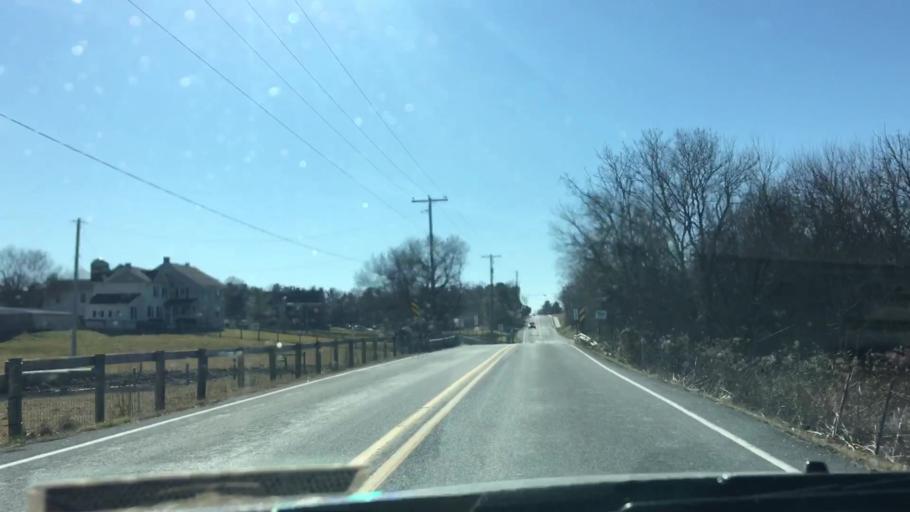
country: US
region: Pennsylvania
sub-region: Lancaster County
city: Lancaster
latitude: 40.0591
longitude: -76.2530
